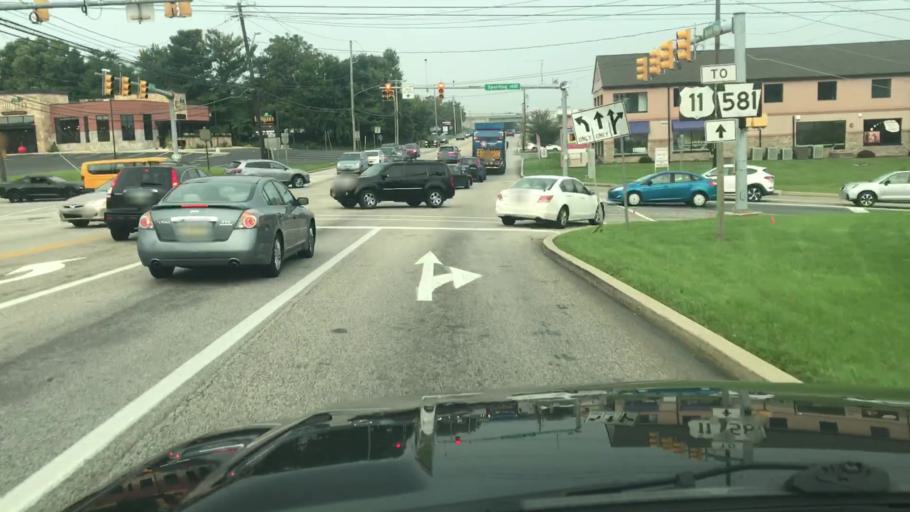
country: US
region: Pennsylvania
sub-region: Cumberland County
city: Shiremanstown
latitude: 40.2372
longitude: -76.9716
